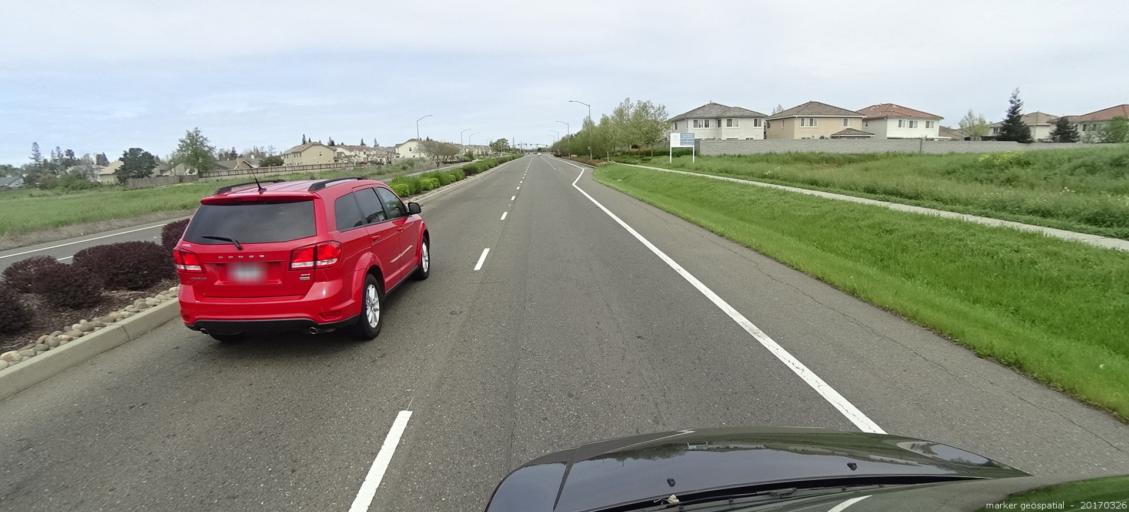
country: US
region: California
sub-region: Sacramento County
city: Laguna
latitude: 38.4400
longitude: -121.4177
